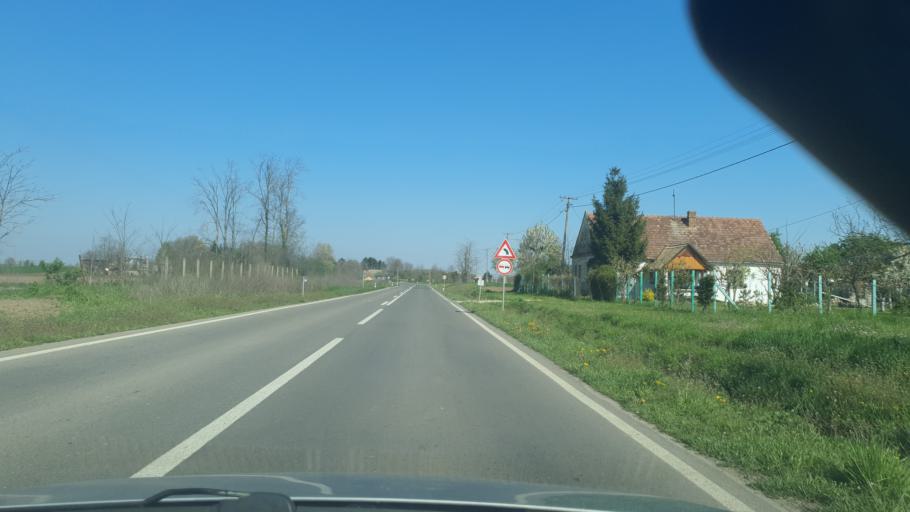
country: RS
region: Autonomna Pokrajina Vojvodina
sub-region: Zapadnobacki Okrug
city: Sombor
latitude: 45.8067
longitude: 19.0516
